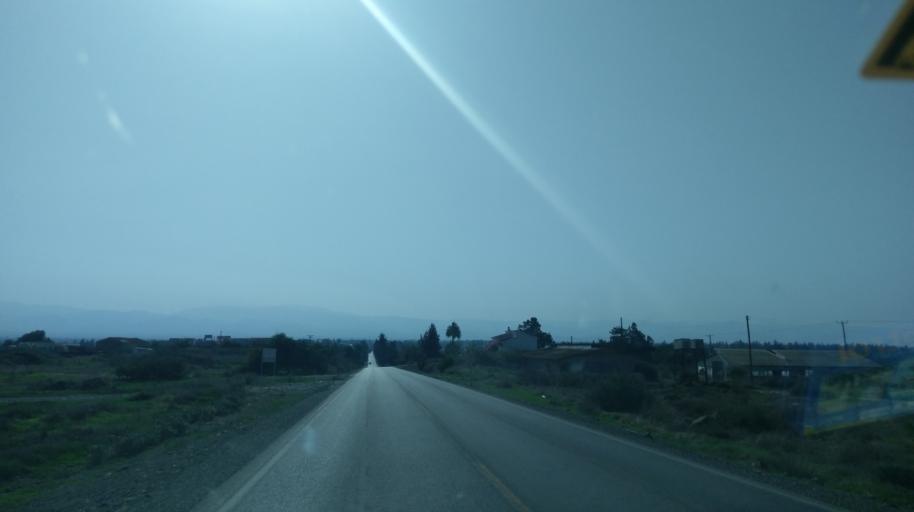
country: CY
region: Lefkosia
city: Morfou
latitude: 35.2277
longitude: 33.0127
